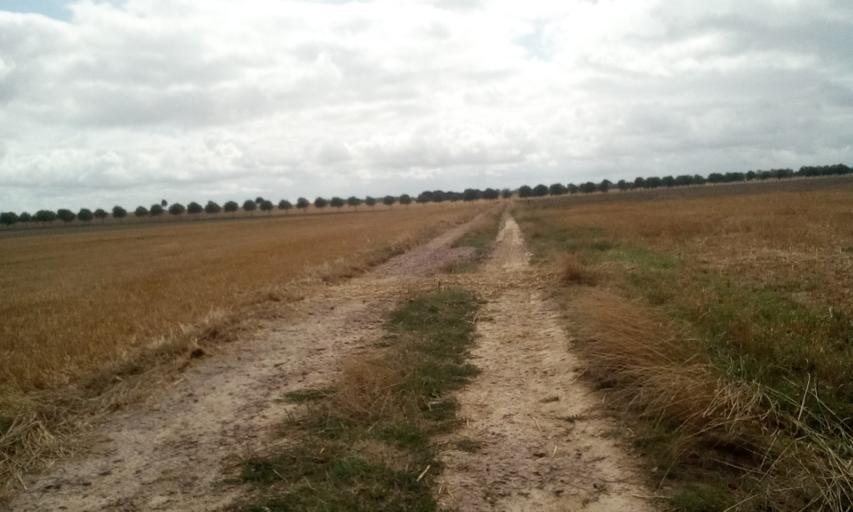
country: FR
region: Lower Normandy
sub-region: Departement du Calvados
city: Cheux
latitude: 49.1798
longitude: -0.5430
